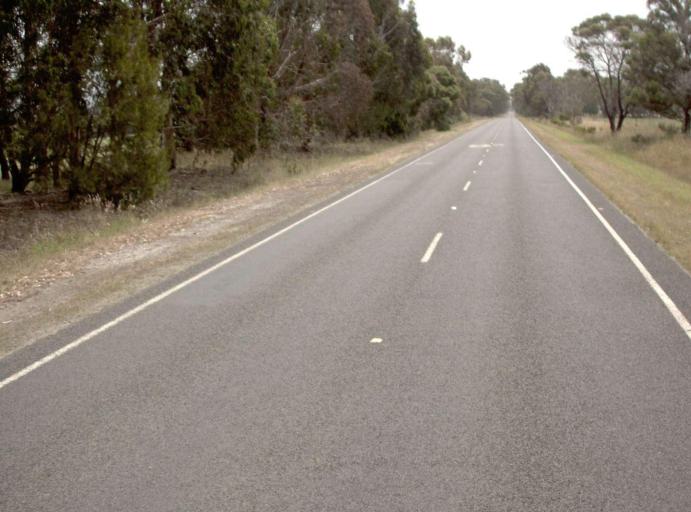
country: AU
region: Victoria
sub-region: Latrobe
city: Traralgon
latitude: -38.4939
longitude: 146.7126
